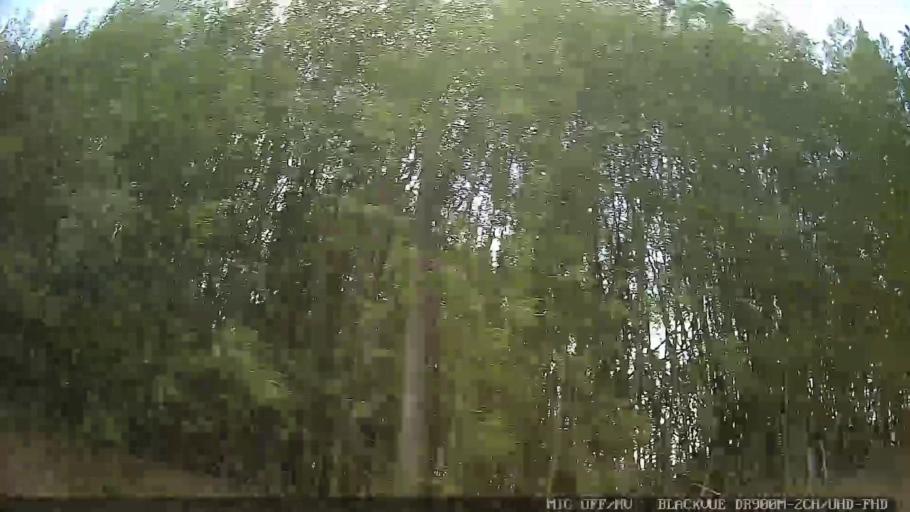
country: BR
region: Sao Paulo
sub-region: Louveira
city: Louveira
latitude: -23.1234
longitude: -46.9639
